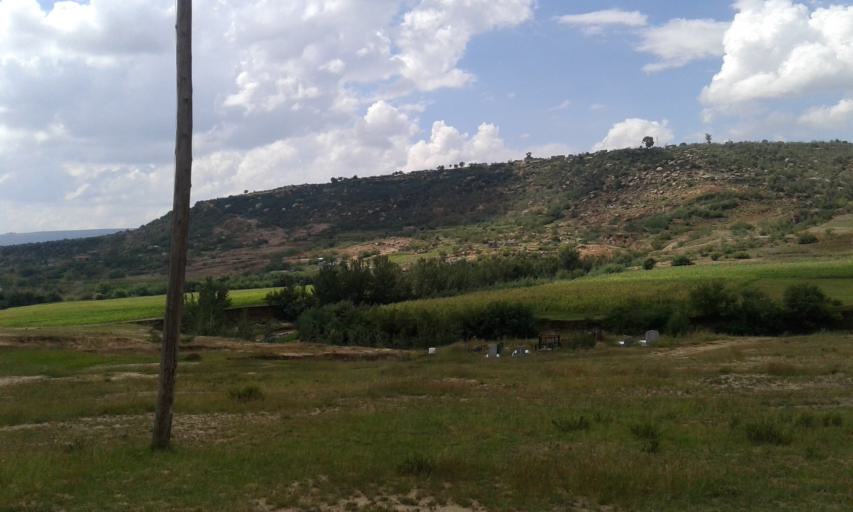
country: LS
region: Maseru
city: Maseru
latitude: -29.4157
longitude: 27.5705
